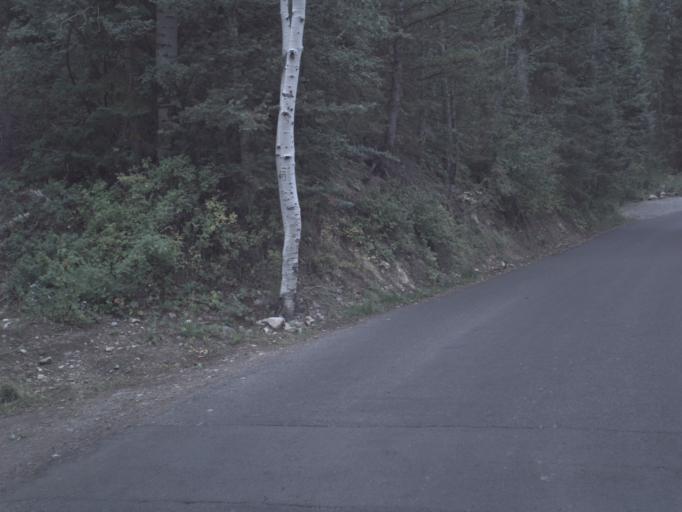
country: US
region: Utah
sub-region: Utah County
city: Lindon
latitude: 40.4351
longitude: -111.6299
